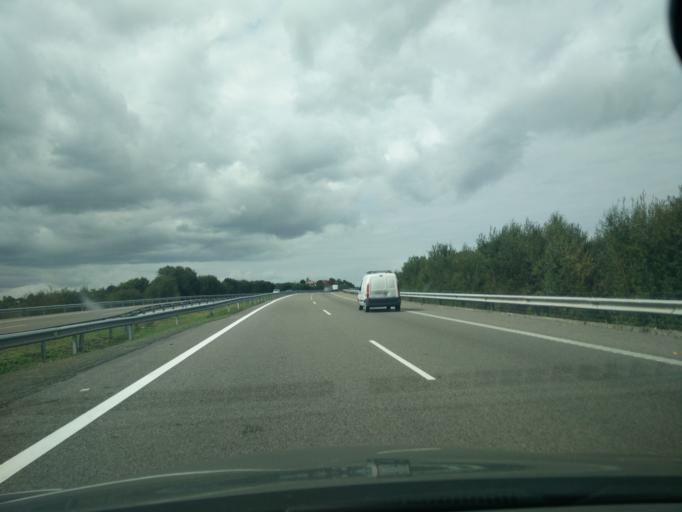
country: ES
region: Galicia
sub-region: Provincia da Coruna
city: Oleiros
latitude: 43.2968
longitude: -8.3090
